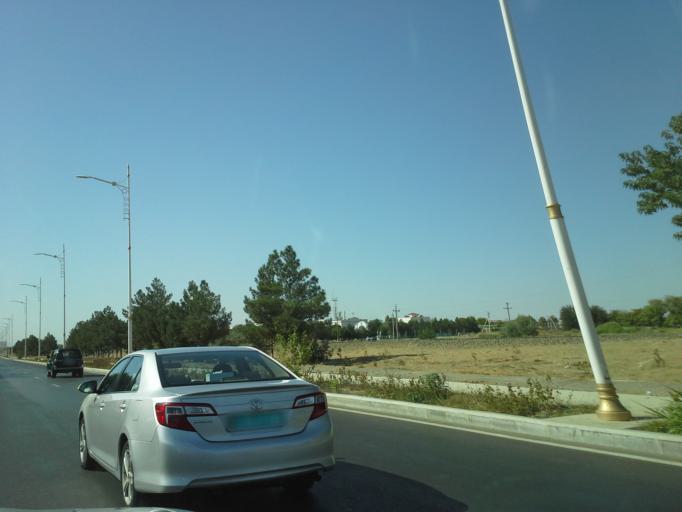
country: TM
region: Ahal
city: Ashgabat
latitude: 37.9212
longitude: 58.4455
